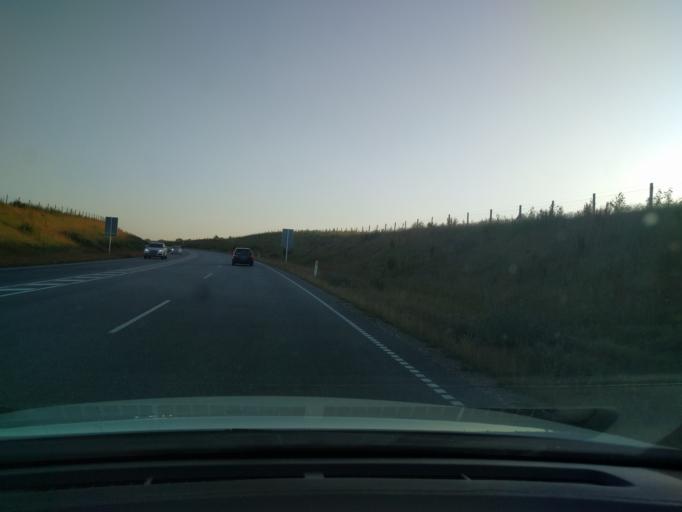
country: DK
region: Zealand
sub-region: Naestved Kommune
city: Naestved
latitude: 55.2634
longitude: 11.7479
